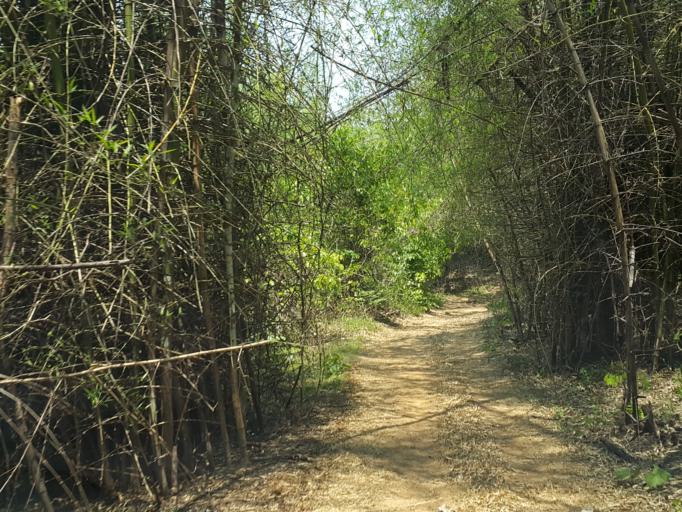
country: TH
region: Kanchanaburi
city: Sai Yok
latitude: 14.2128
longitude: 98.8786
